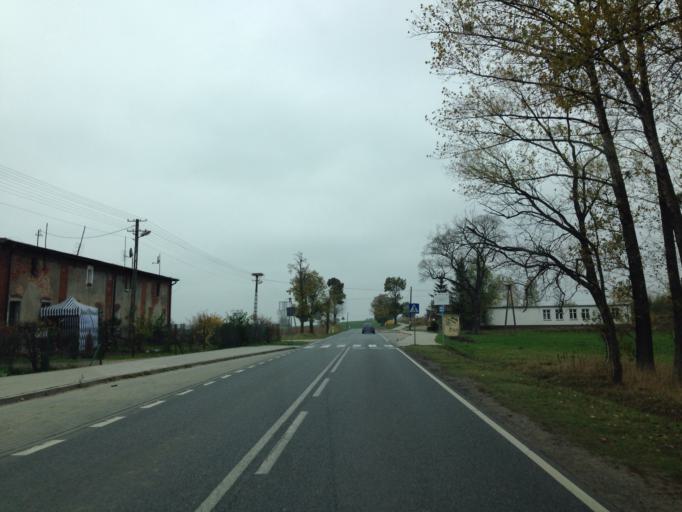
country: PL
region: Kujawsko-Pomorskie
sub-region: Powiat grudziadzki
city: Radzyn Chelminski
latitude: 53.3810
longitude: 18.9766
